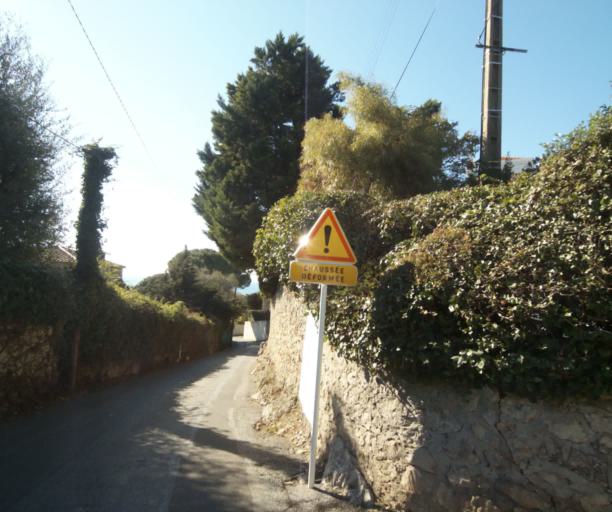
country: FR
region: Provence-Alpes-Cote d'Azur
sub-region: Departement des Alpes-Maritimes
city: Antibes
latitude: 43.5631
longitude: 7.1194
